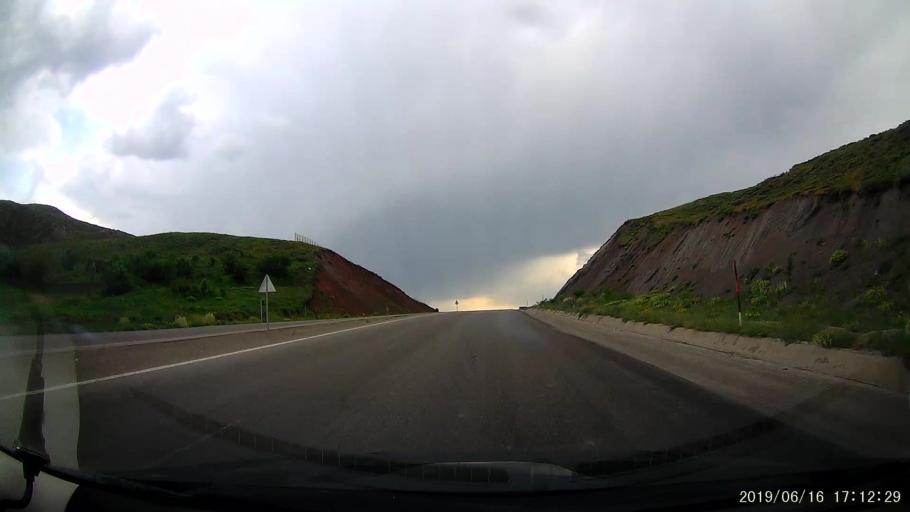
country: TR
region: Erzurum
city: Askale
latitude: 39.8593
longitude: 40.6181
